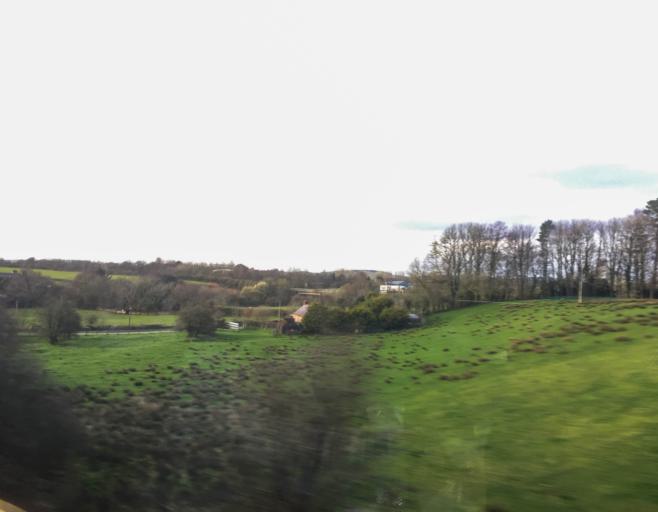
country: GB
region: Scotland
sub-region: Dumfries and Galloway
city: Annan
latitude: 55.0428
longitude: -3.1909
